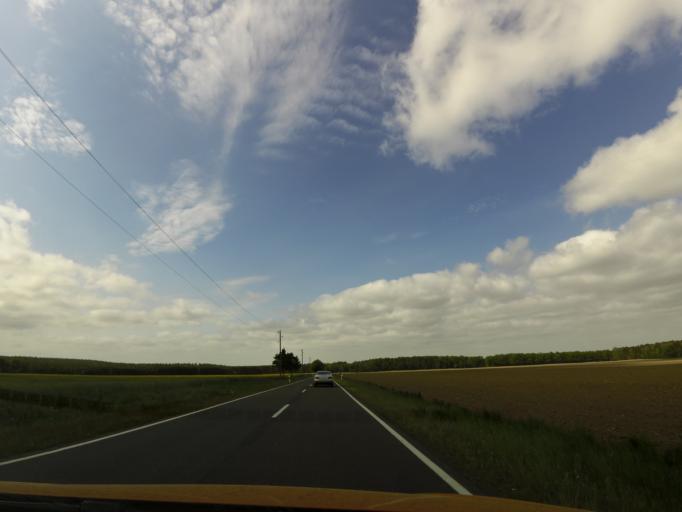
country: DE
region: Brandenburg
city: Gorzke
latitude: 52.1019
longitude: 12.3524
